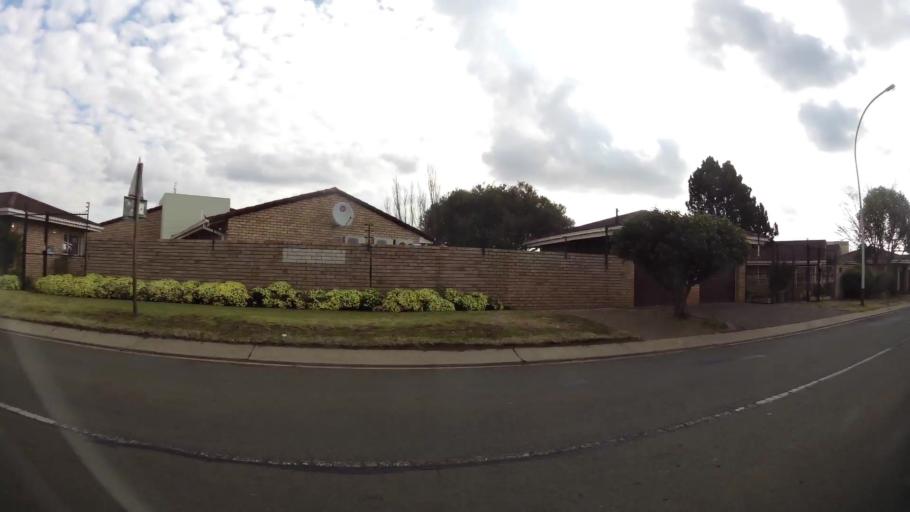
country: ZA
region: Orange Free State
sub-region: Mangaung Metropolitan Municipality
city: Bloemfontein
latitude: -29.0757
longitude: 26.2083
